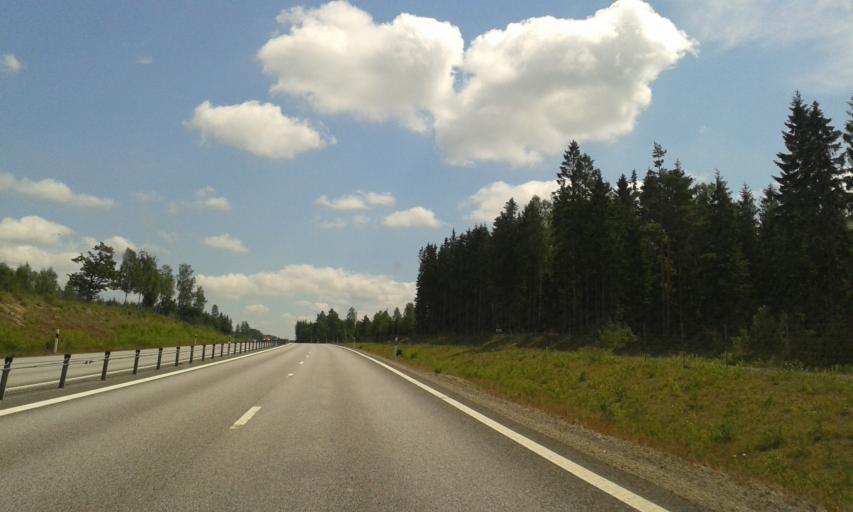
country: SE
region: Kronoberg
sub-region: Vaxjo Kommun
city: Gemla
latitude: 56.9100
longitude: 14.6400
